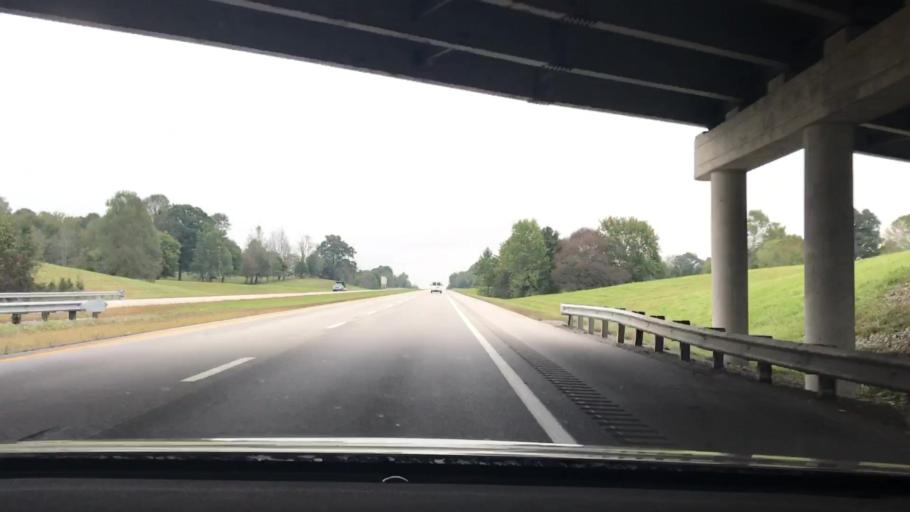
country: US
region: Kentucky
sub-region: Pulaski County
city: Somerset
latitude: 37.0926
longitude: -84.8007
